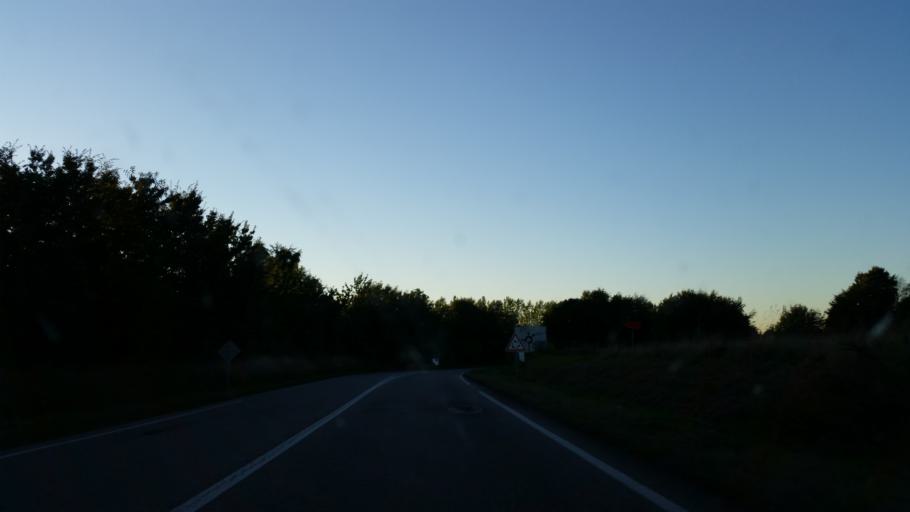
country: FR
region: Lower Normandy
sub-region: Departement du Calvados
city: La Riviere-Saint-Sauveur
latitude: 49.3920
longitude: 0.2499
